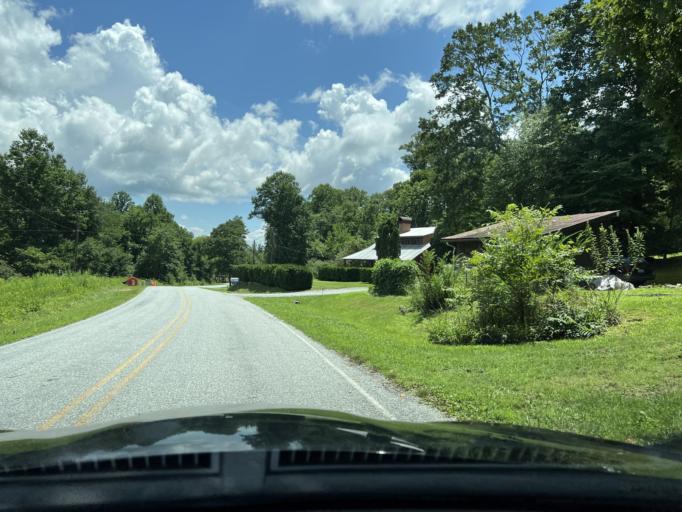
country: US
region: North Carolina
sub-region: Henderson County
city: Fruitland
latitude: 35.4151
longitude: -82.4002
